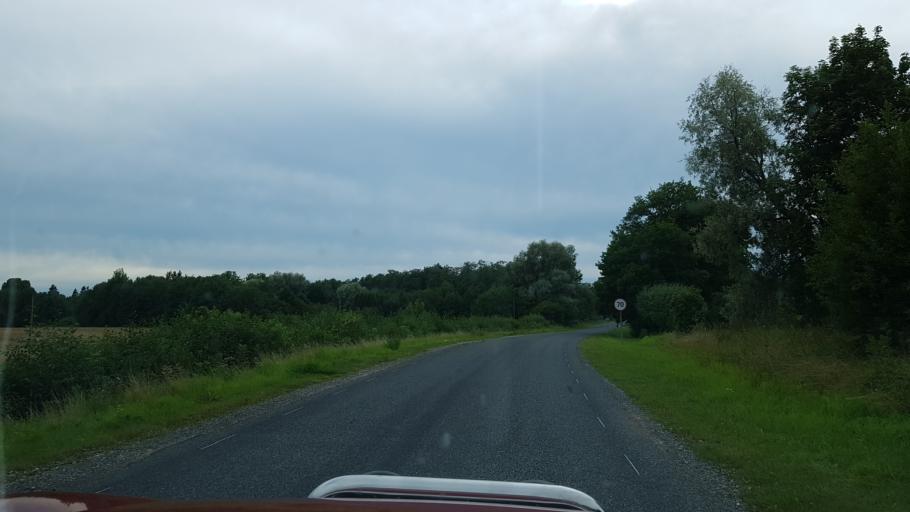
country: EE
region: Laeaene
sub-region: Lihula vald
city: Lihula
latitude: 58.8559
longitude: 23.8096
